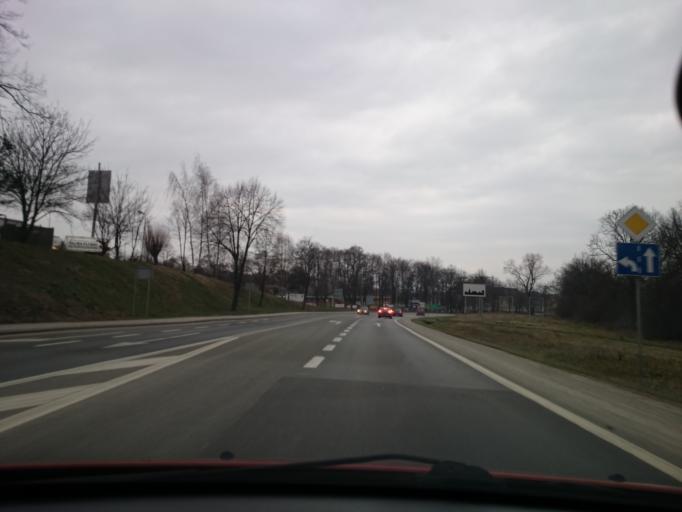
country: PL
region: Opole Voivodeship
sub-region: Powiat nyski
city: Nysa
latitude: 50.4950
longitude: 17.3481
